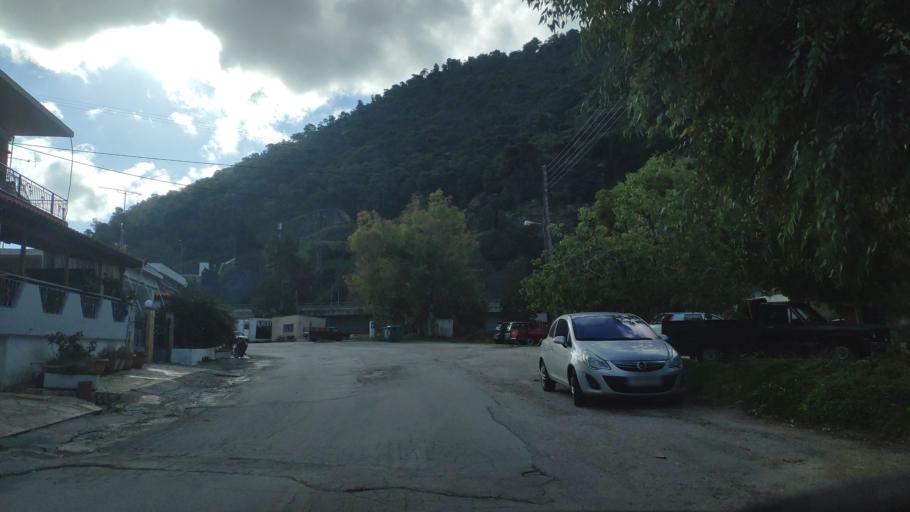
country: GR
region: West Greece
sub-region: Nomos Achaias
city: Aiyira
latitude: 38.1324
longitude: 22.4279
